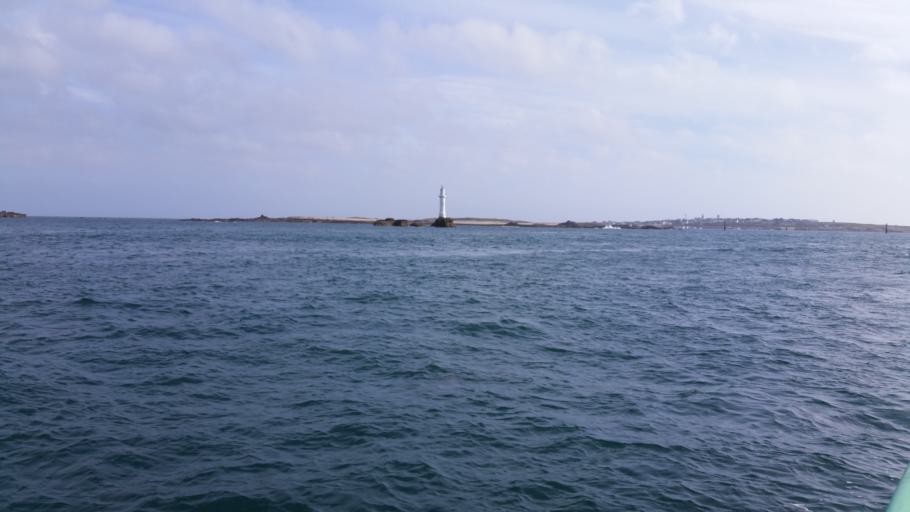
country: FR
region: Brittany
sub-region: Departement du Finistere
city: Le Conquet
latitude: 48.4148
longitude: -4.9470
